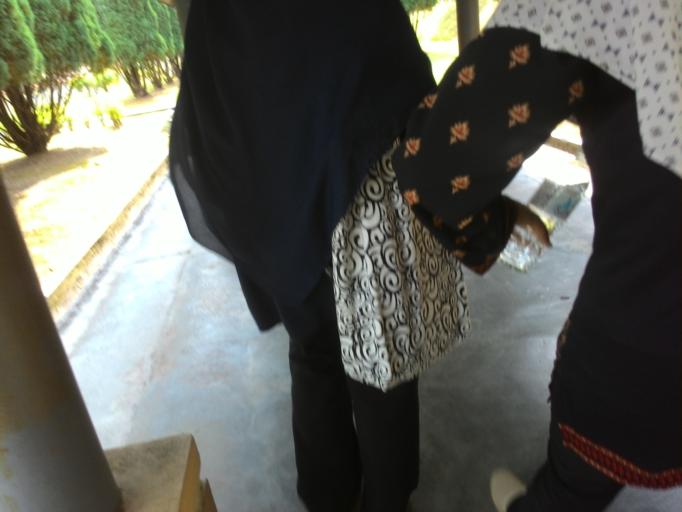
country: MY
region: Kedah
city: Kulim
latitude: 5.3838
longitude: 100.5777
